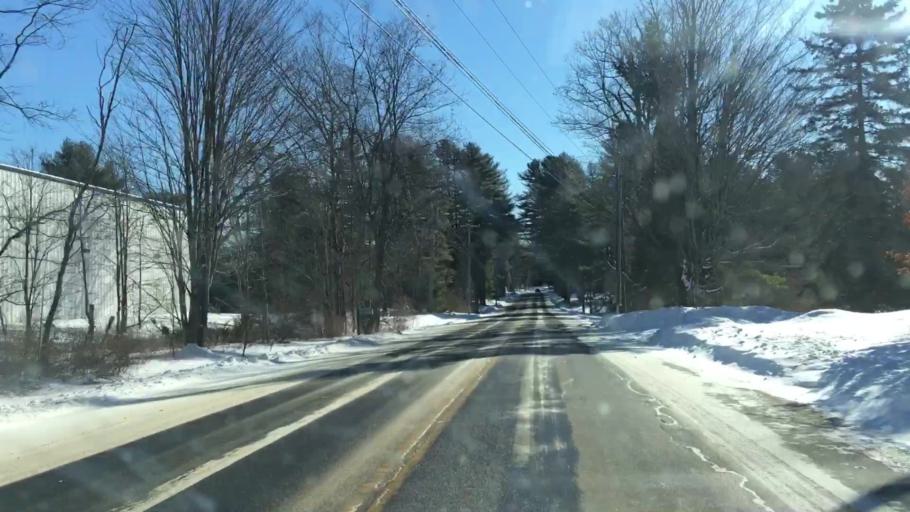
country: US
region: Maine
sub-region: Sagadahoc County
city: Topsham
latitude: 43.9045
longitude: -70.0010
